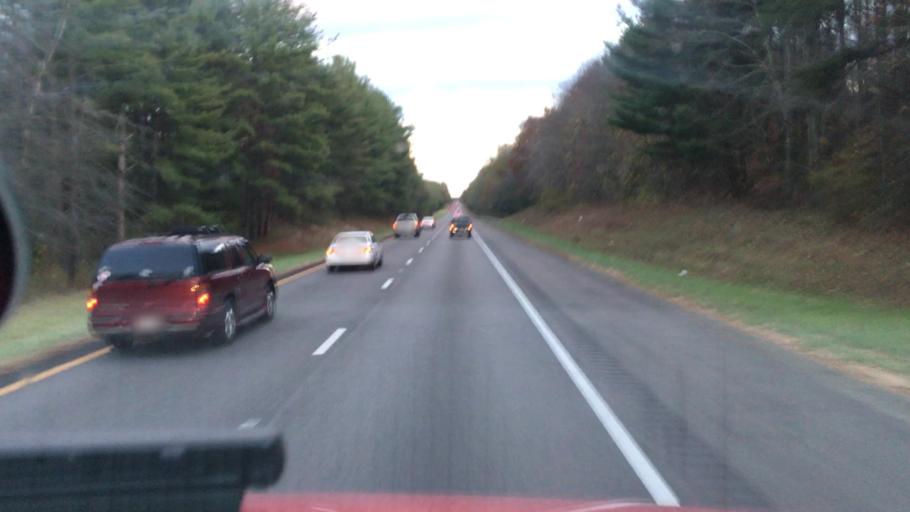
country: US
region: Virginia
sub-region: Fluvanna County
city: Palmyra
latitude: 37.9575
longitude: -78.1607
